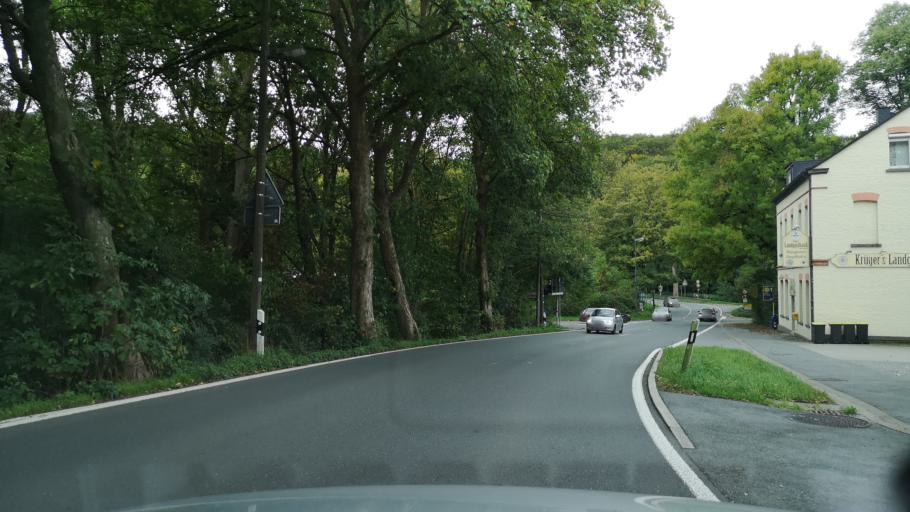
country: DE
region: North Rhine-Westphalia
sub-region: Regierungsbezirk Dusseldorf
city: Velbert
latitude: 51.3837
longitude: 7.0386
